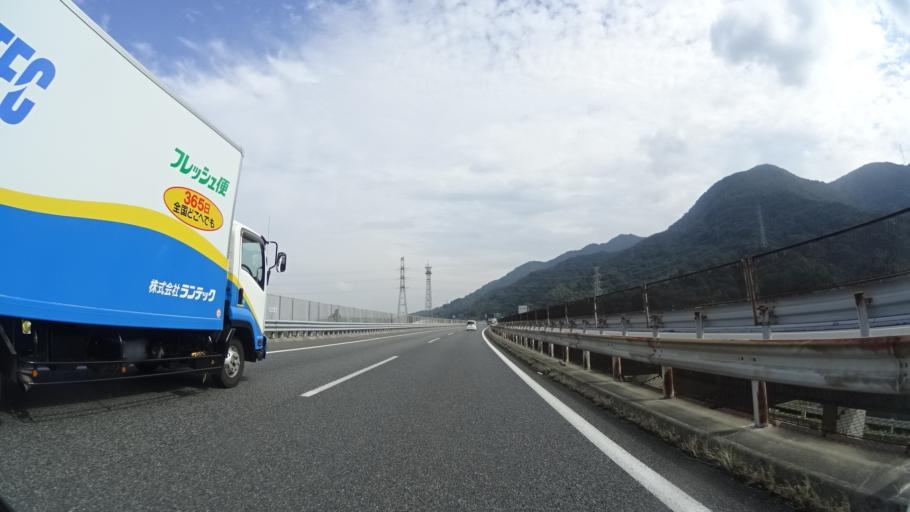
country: JP
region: Kumamoto
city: Yatsushiro
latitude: 32.5198
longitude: 130.6534
